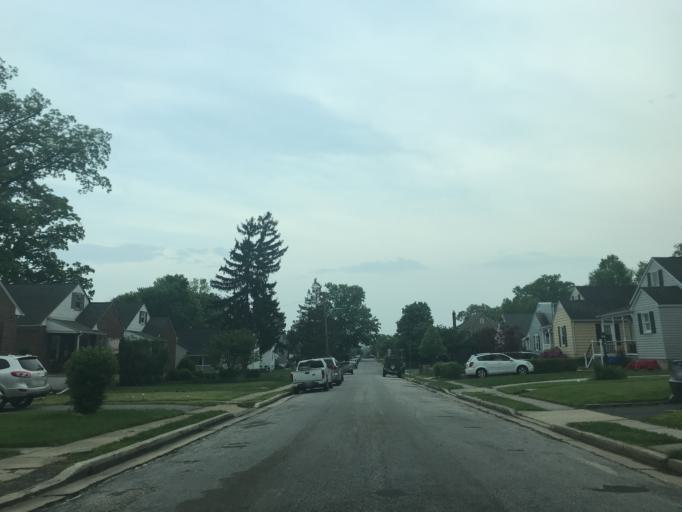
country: US
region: Maryland
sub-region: Baltimore County
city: Parkville
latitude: 39.3809
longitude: -76.5411
